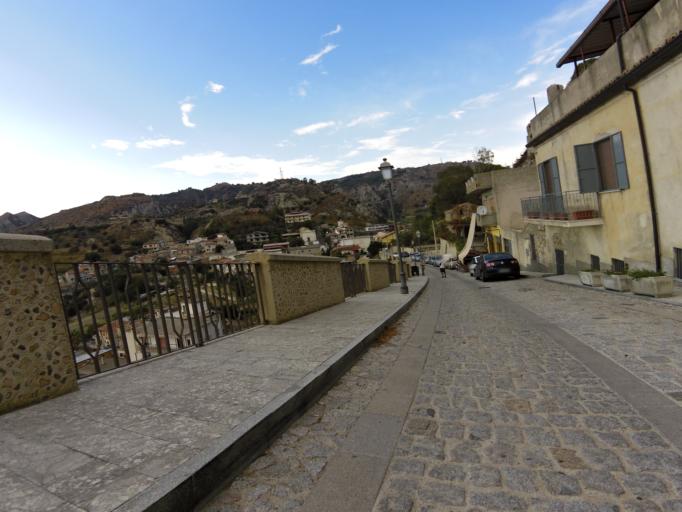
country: IT
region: Calabria
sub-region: Provincia di Reggio Calabria
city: Roccella Ionica
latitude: 38.3261
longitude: 16.4069
